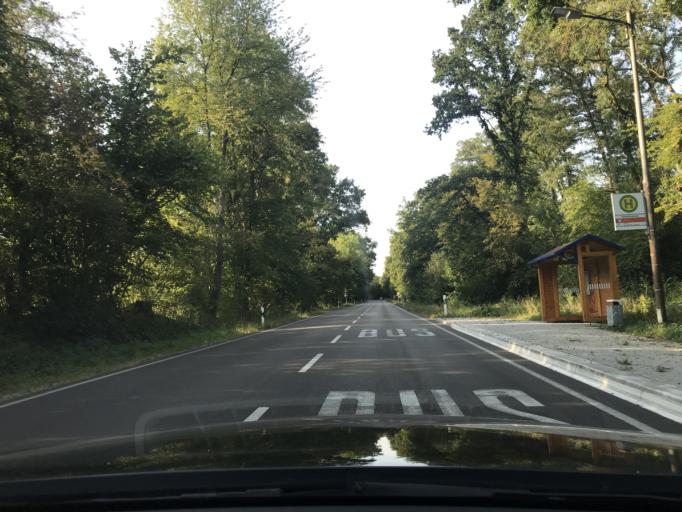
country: DE
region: Baden-Wuerttemberg
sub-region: Regierungsbezirk Stuttgart
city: Ostfildern
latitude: 48.7330
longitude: 9.2074
